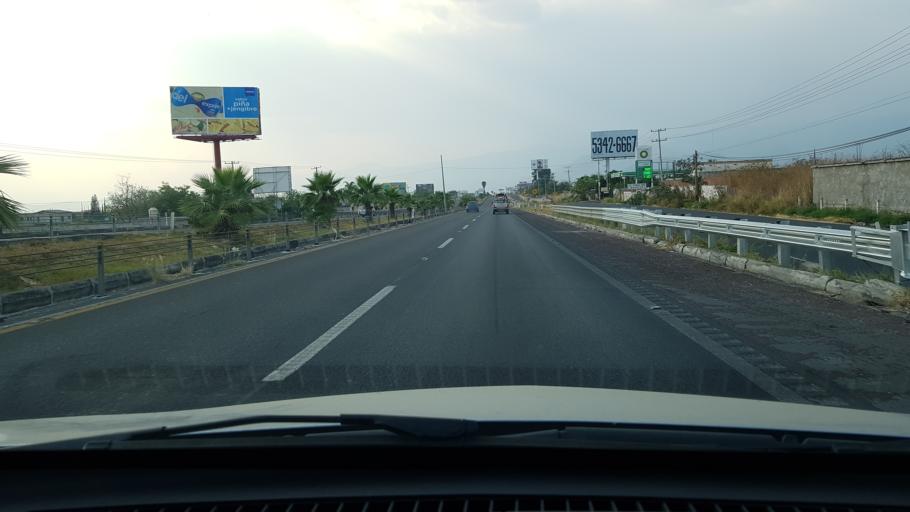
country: MX
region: Morelos
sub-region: Cuautla
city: Tierra Larga (Campo Nuevo)
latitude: 18.8569
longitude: -98.9422
